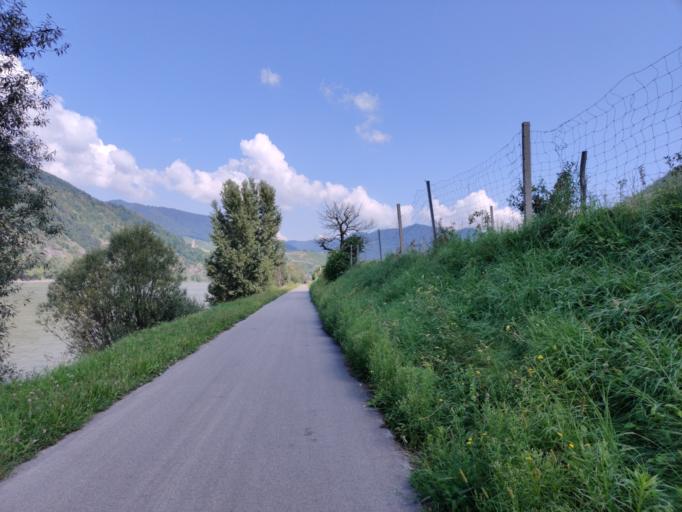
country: AT
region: Lower Austria
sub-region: Politischer Bezirk Krems
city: Spitz
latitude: 48.3461
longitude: 15.4098
